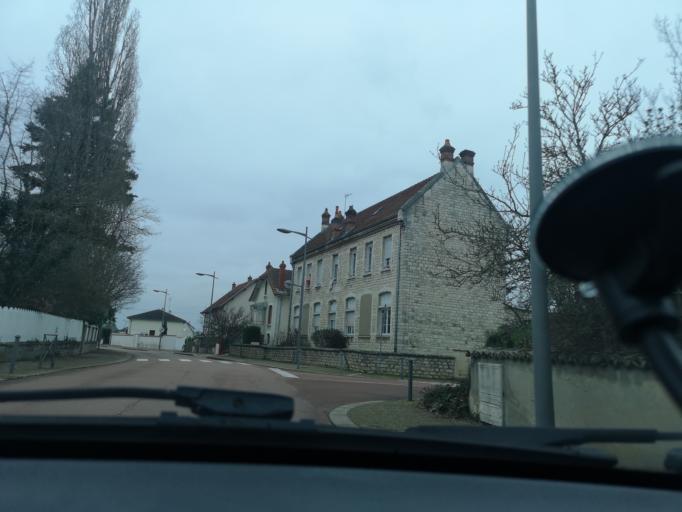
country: FR
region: Bourgogne
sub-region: Departement de Saone-et-Loire
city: Chatenoy-le-Royal
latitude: 46.7901
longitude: 4.8097
